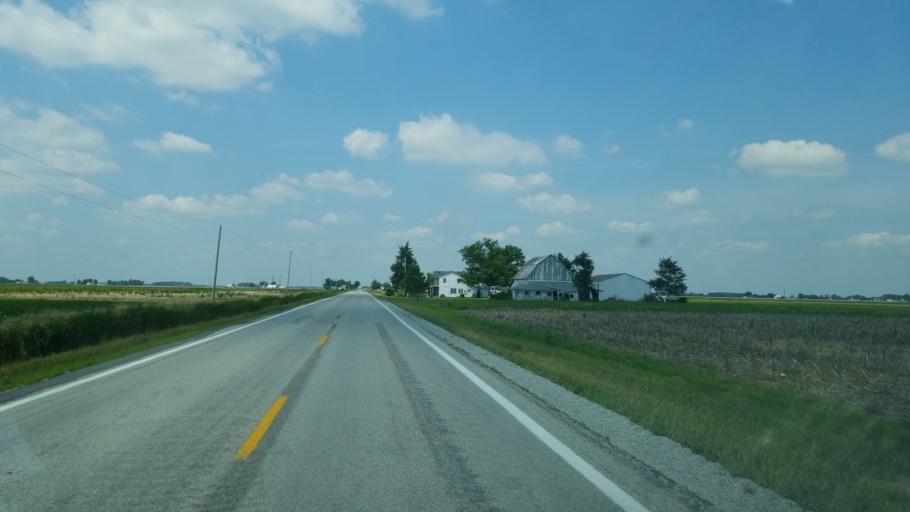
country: US
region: Ohio
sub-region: Henry County
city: Deshler
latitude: 41.2840
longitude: -83.9156
